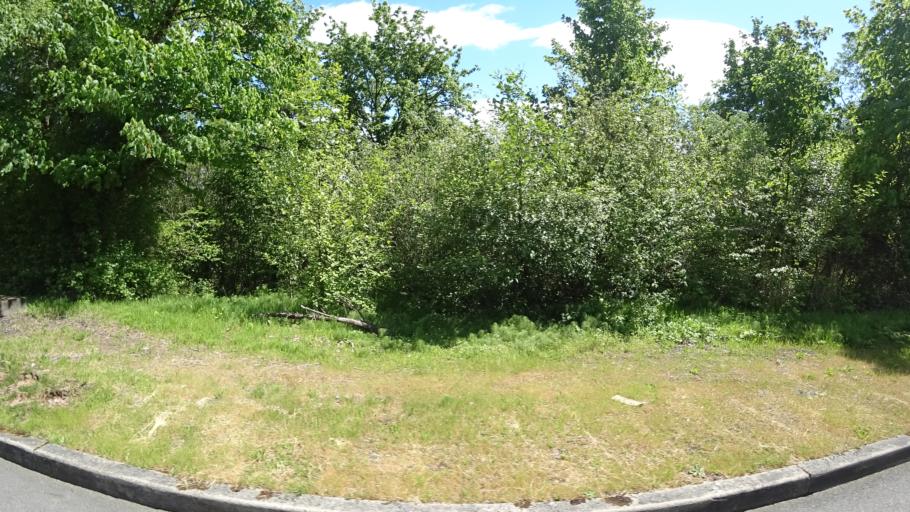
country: US
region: Oregon
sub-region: Washington County
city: West Haven
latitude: 45.5485
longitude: -122.7794
